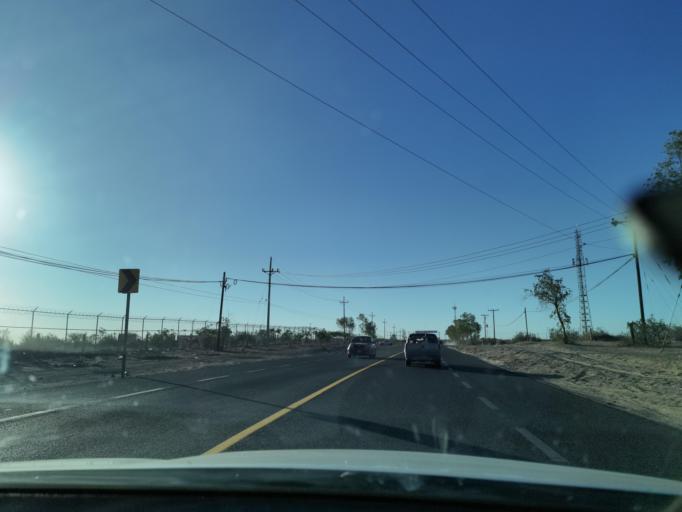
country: MX
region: Baja California
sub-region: Mexicali
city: Islas Agrarias Grupo A
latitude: 32.6297
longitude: -115.2560
